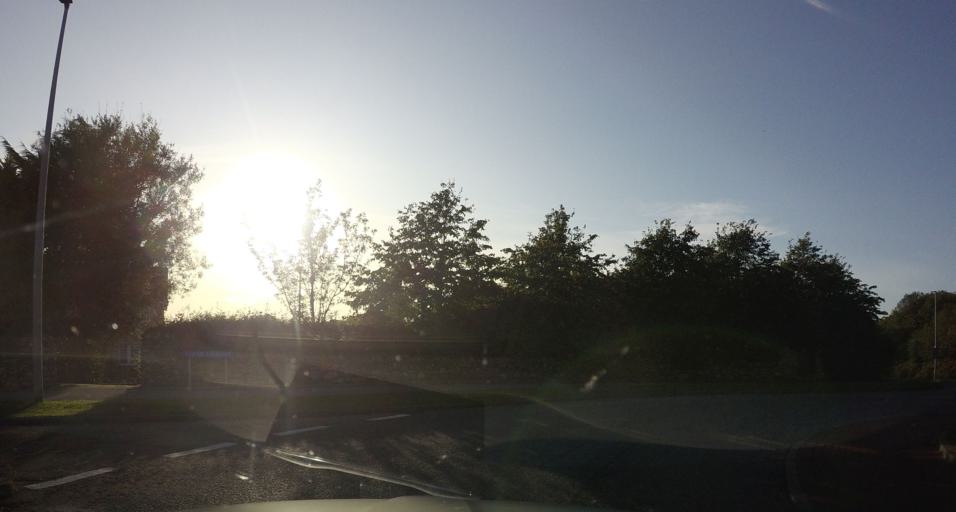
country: GB
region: Scotland
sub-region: Aberdeenshire
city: Westhill
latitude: 57.1508
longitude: -2.3028
